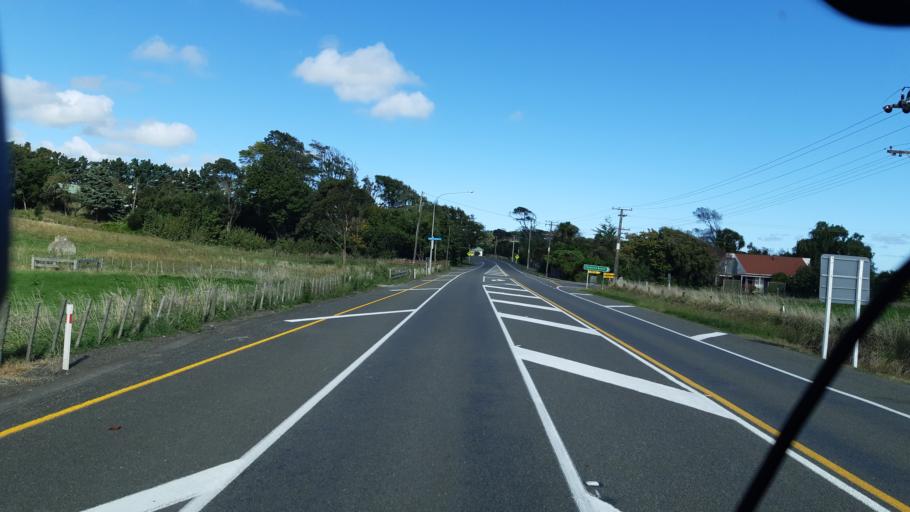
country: NZ
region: Manawatu-Wanganui
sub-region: Wanganui District
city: Wanganui
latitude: -40.0406
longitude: 175.2120
